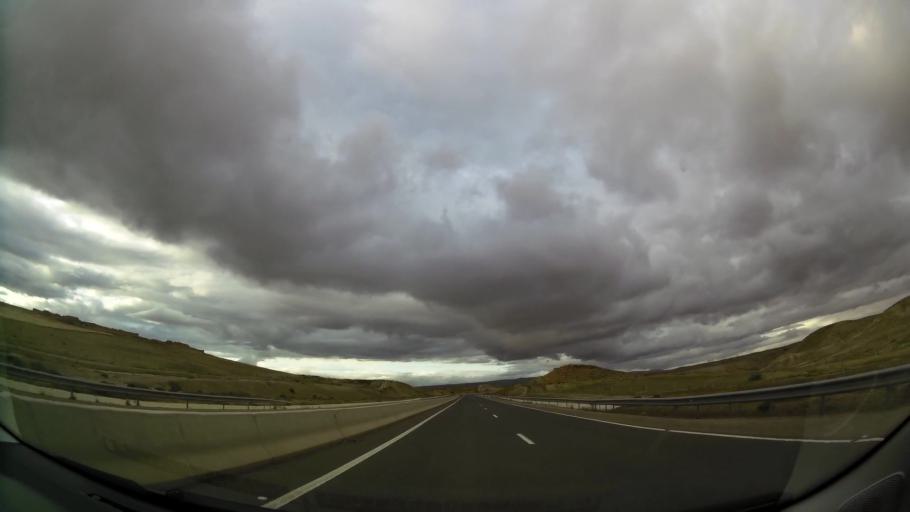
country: MA
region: Taza-Al Hoceima-Taounate
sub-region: Taza
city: Taza
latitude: 34.2940
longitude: -3.7797
